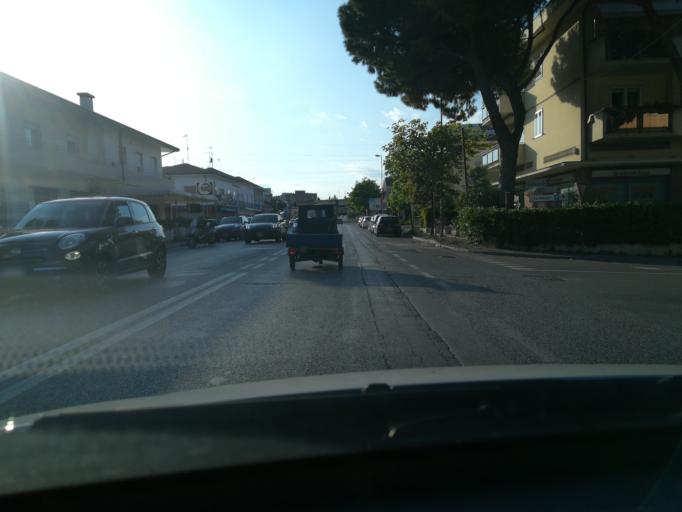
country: IT
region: Emilia-Romagna
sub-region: Provincia di Rimini
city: Riccione
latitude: 43.9918
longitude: 12.6642
